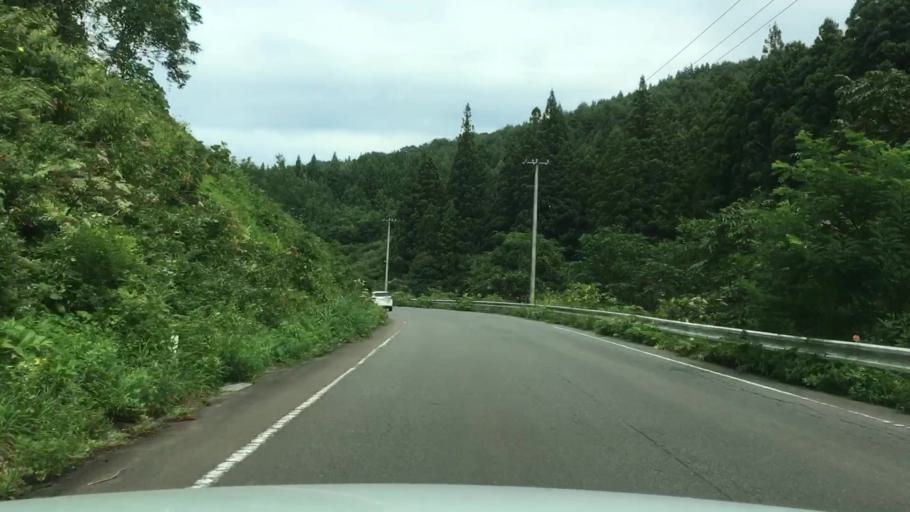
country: JP
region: Aomori
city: Shimokizukuri
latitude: 40.7407
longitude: 140.2448
